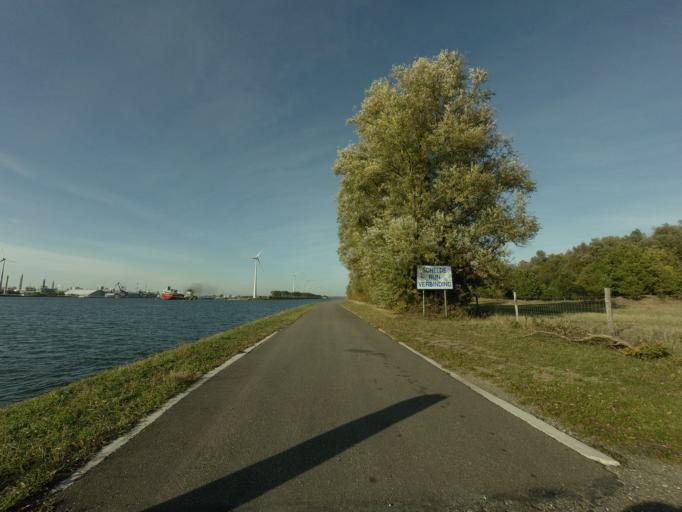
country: BE
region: Flanders
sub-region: Provincie Antwerpen
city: Stabroek
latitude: 51.3457
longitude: 4.3022
